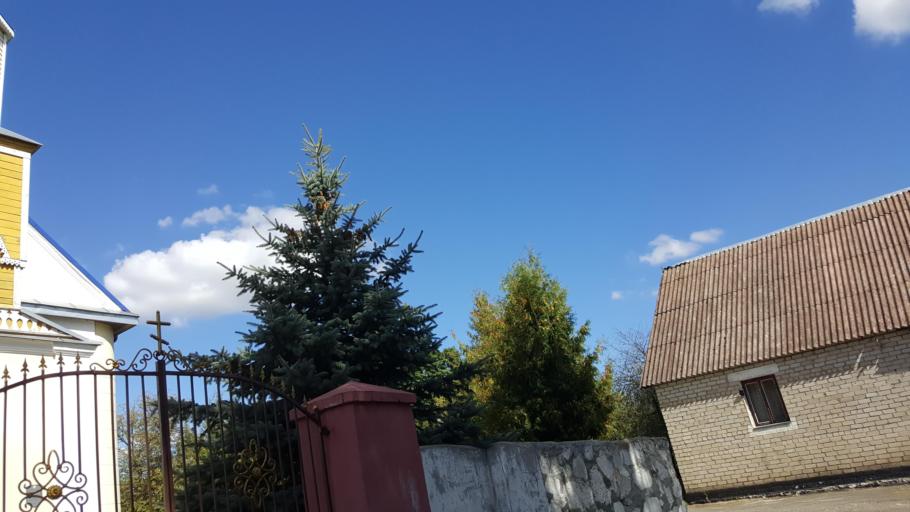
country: BY
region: Brest
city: Vysokaye
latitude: 52.2826
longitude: 23.3125
